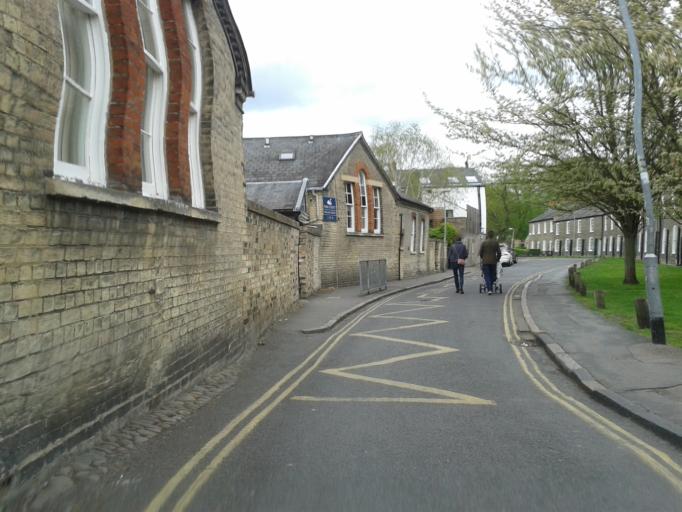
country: GB
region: England
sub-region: Cambridgeshire
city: Cambridge
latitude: 52.2097
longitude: 0.1197
